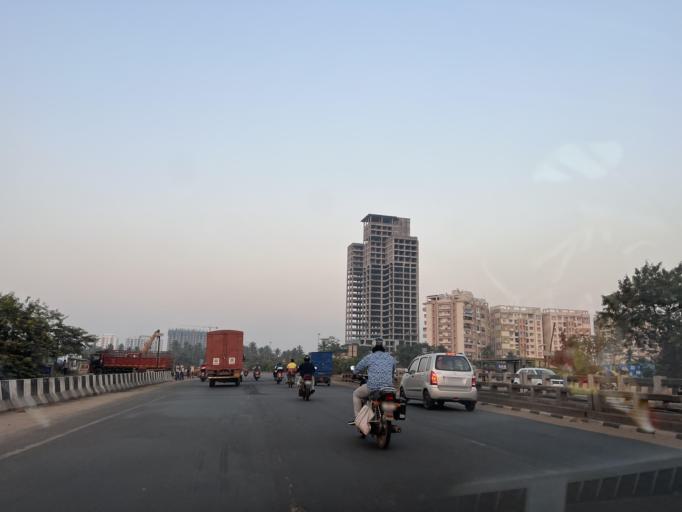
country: IN
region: Odisha
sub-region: Khordha
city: Bhubaneshwar
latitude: 20.3194
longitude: 85.8810
